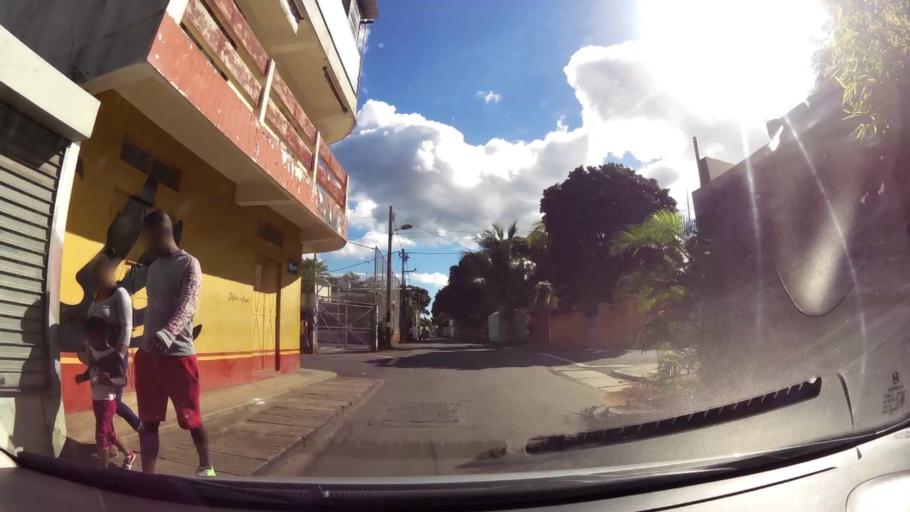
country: MU
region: Pamplemousses
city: Le Hochet
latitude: -20.1454
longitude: 57.5195
